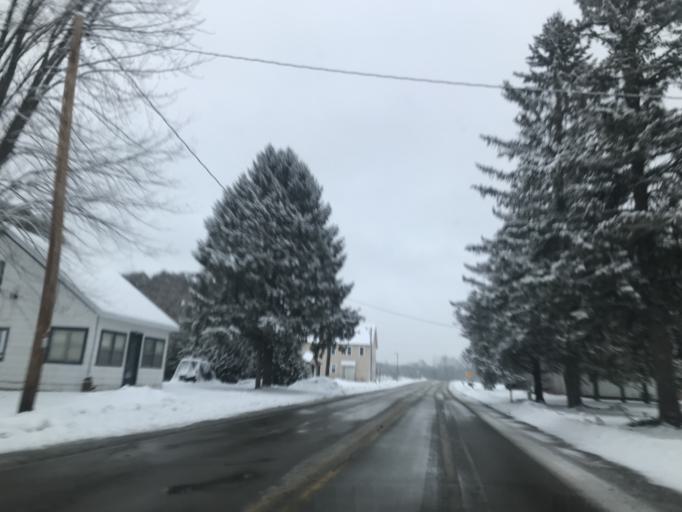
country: US
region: Wisconsin
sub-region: Oconto County
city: Oconto Falls
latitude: 44.8618
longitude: -88.0518
